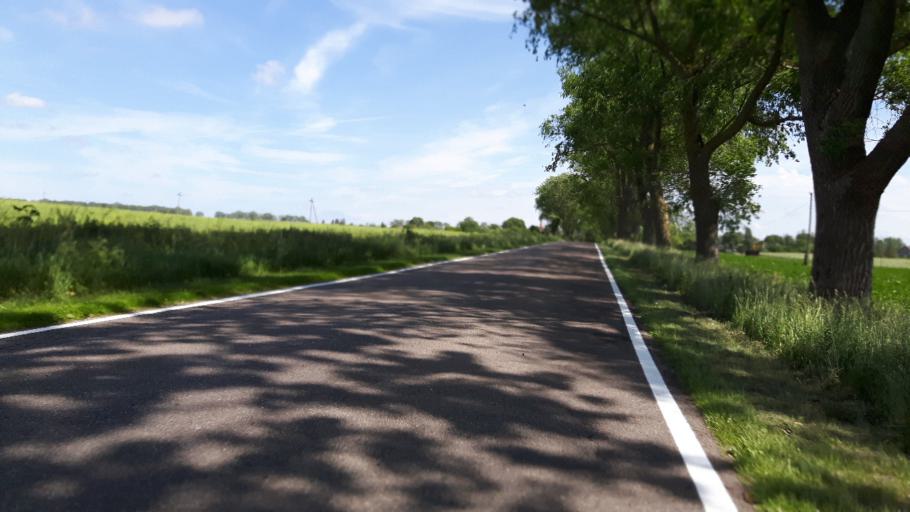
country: PL
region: Pomeranian Voivodeship
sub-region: Powiat wejherowski
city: Gniewino
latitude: 54.7192
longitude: 17.9998
